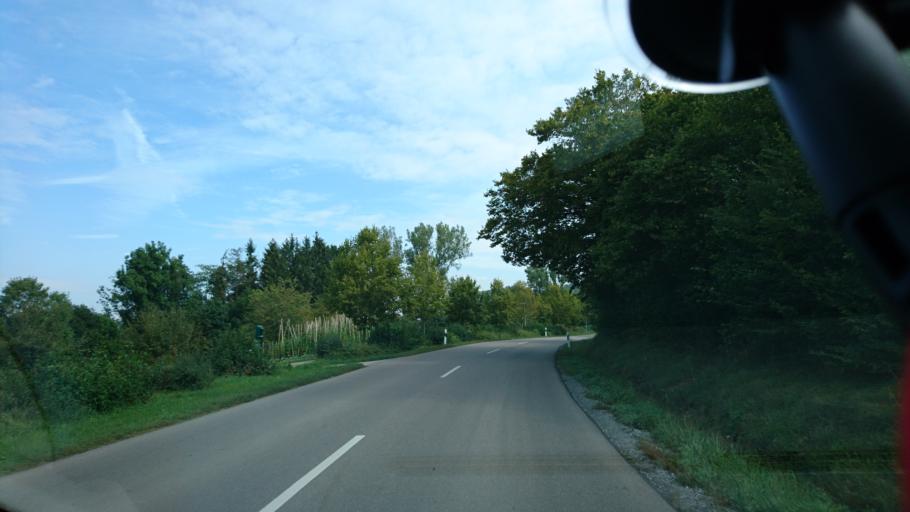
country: DE
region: Baden-Wuerttemberg
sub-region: Regierungsbezirk Stuttgart
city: Vellberg
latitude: 49.0932
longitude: 9.8844
